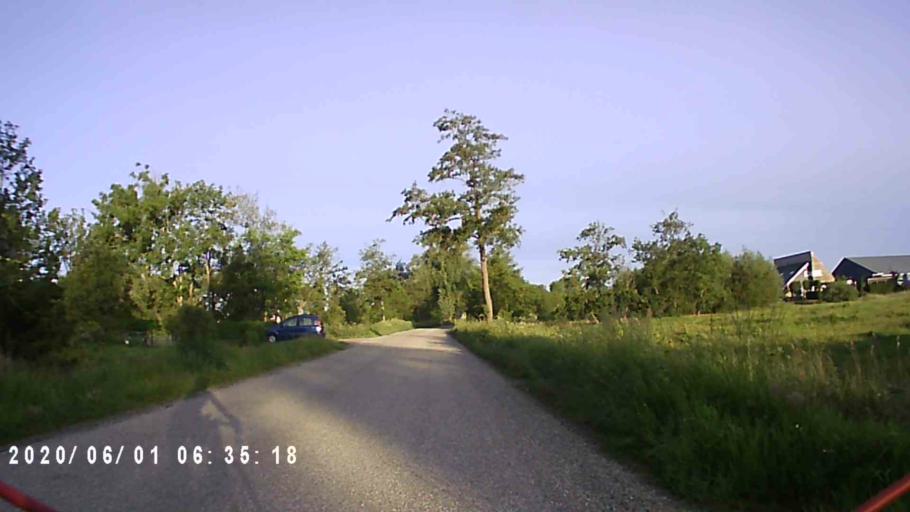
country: NL
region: Friesland
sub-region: Gemeente Kollumerland en Nieuwkruisland
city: Kollum
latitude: 53.2800
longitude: 6.1631
